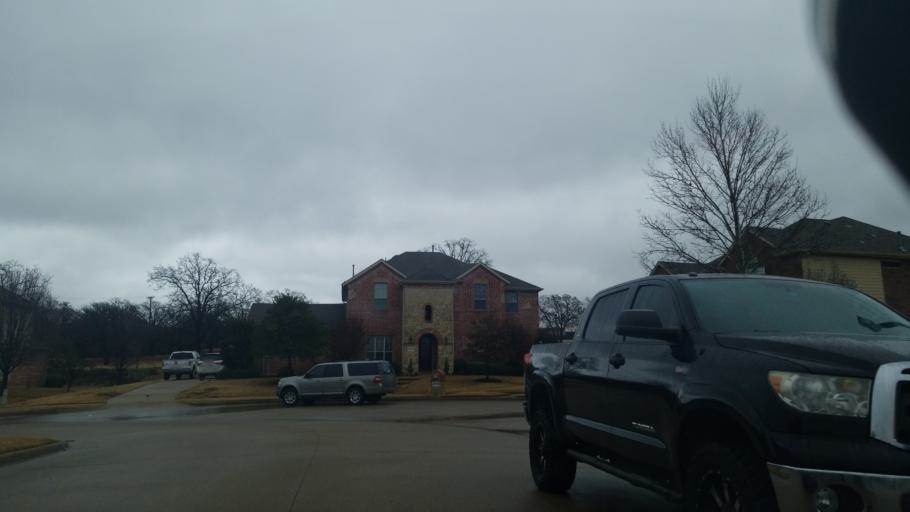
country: US
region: Texas
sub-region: Denton County
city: Corinth
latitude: 33.1411
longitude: -97.0910
